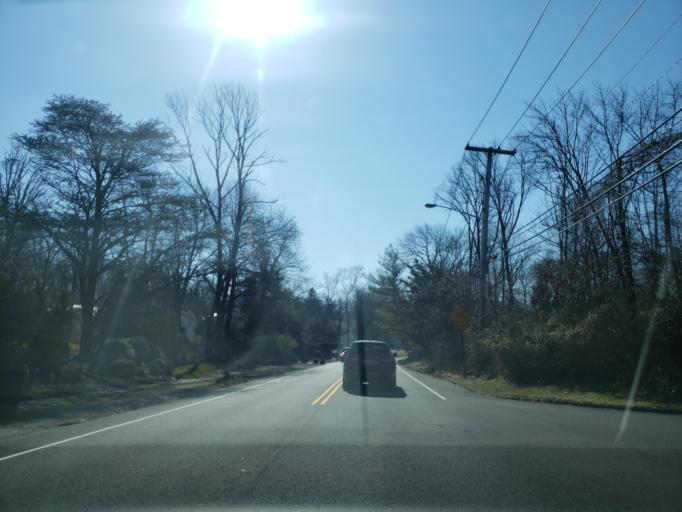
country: US
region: New Jersey
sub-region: Essex County
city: Short Hills
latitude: 40.7491
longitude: -74.3115
